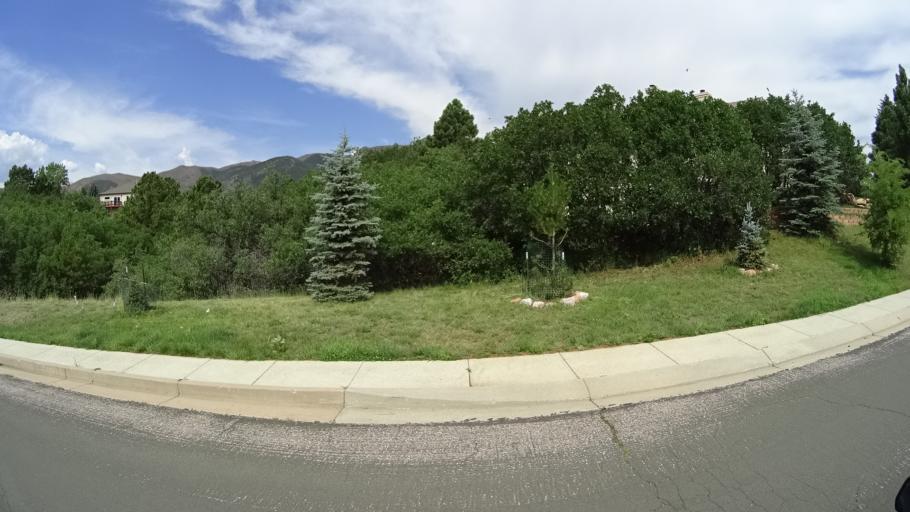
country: US
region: Colorado
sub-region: El Paso County
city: Air Force Academy
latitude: 38.9534
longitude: -104.8714
